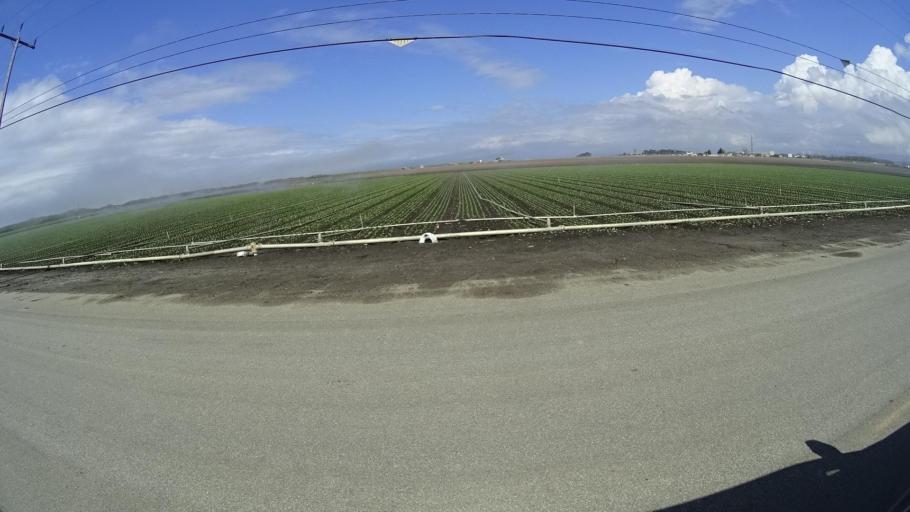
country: US
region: California
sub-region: Monterey County
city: Castroville
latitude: 36.7769
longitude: -121.7815
